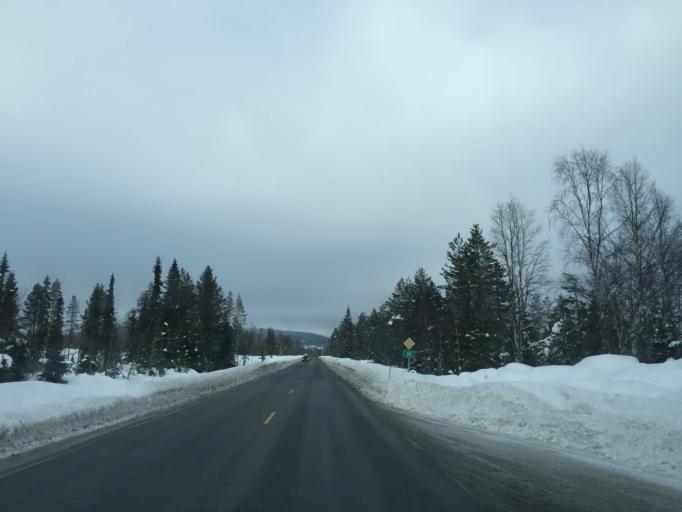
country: NO
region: Hedmark
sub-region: Trysil
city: Innbygda
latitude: 61.1489
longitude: 12.1291
